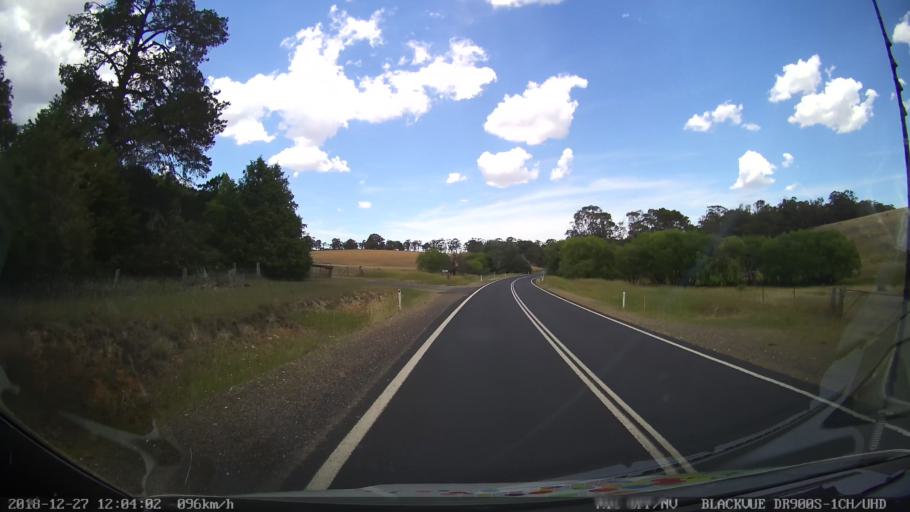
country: AU
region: New South Wales
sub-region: Blayney
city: Blayney
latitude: -33.7927
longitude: 149.3547
